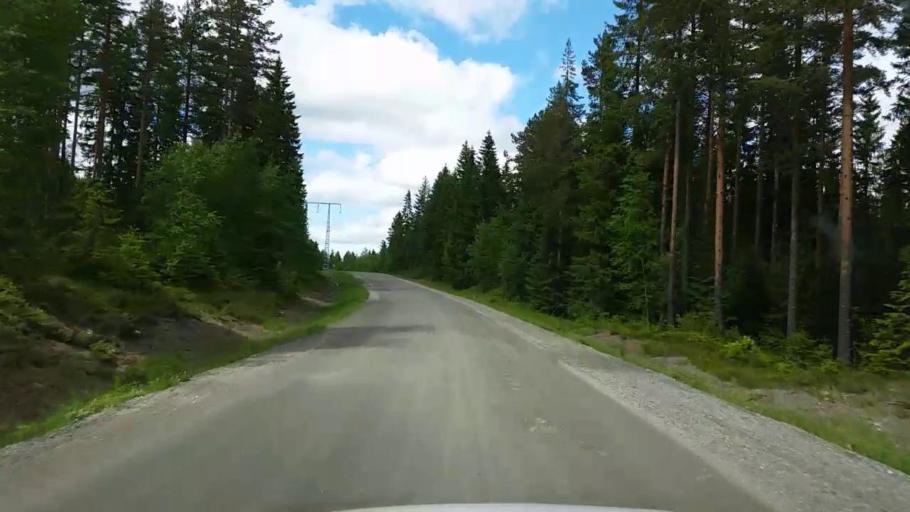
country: SE
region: Gaevleborg
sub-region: Bollnas Kommun
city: Vittsjo
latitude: 61.1754
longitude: 16.1506
